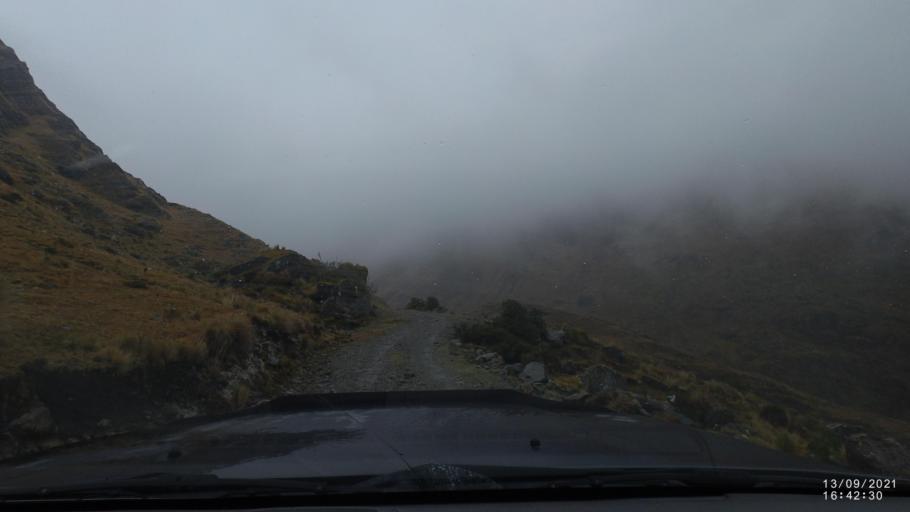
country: BO
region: Cochabamba
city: Colomi
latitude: -17.2873
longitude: -65.7114
